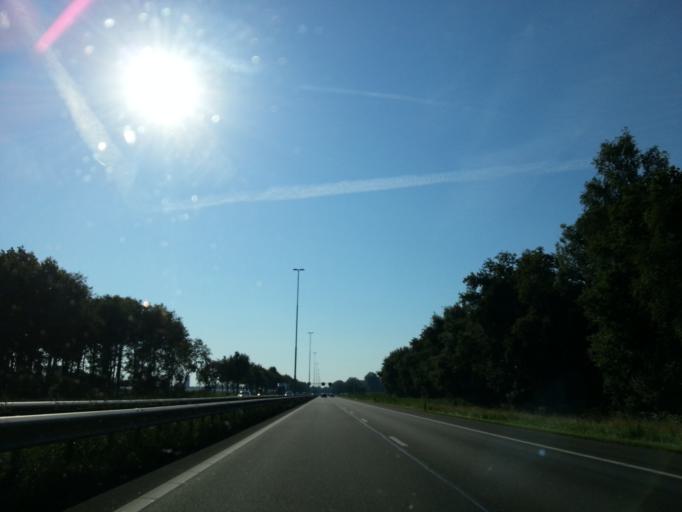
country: NL
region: North Brabant
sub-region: Gemeente Oirschot
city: Oostelbeers
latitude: 51.5079
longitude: 5.2754
